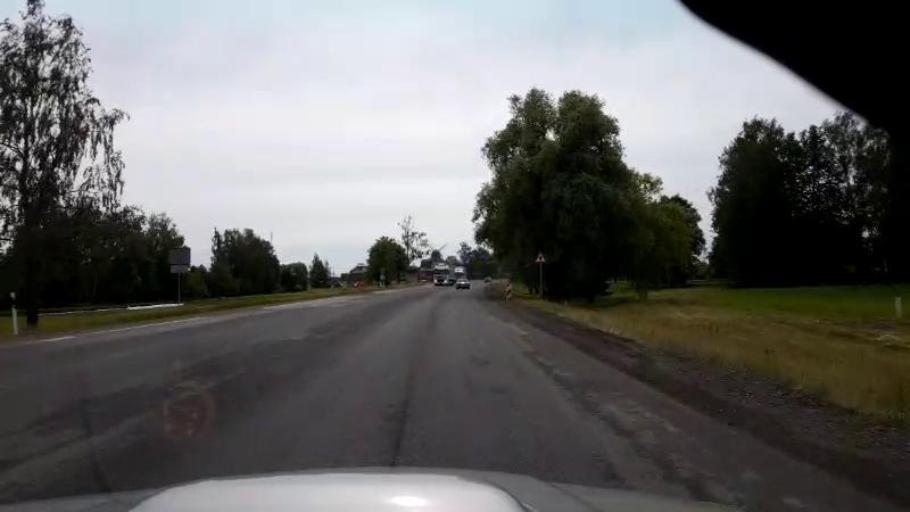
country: LV
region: Bauskas Rajons
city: Bauska
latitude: 56.3608
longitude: 24.2826
